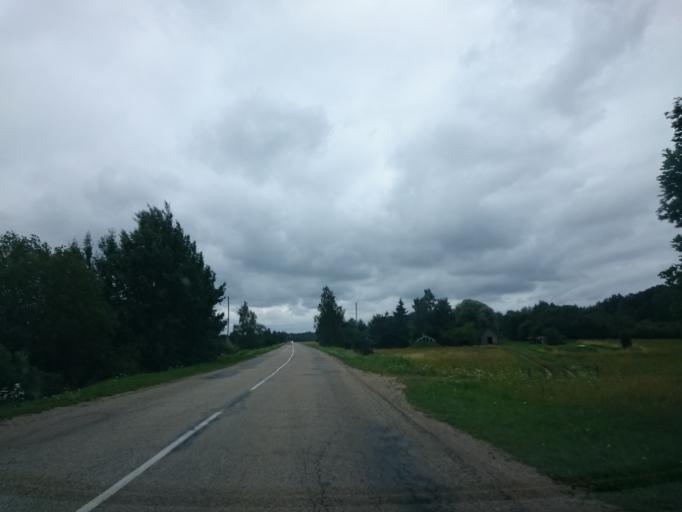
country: LV
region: Pavilostas
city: Pavilosta
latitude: 56.8766
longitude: 21.2239
